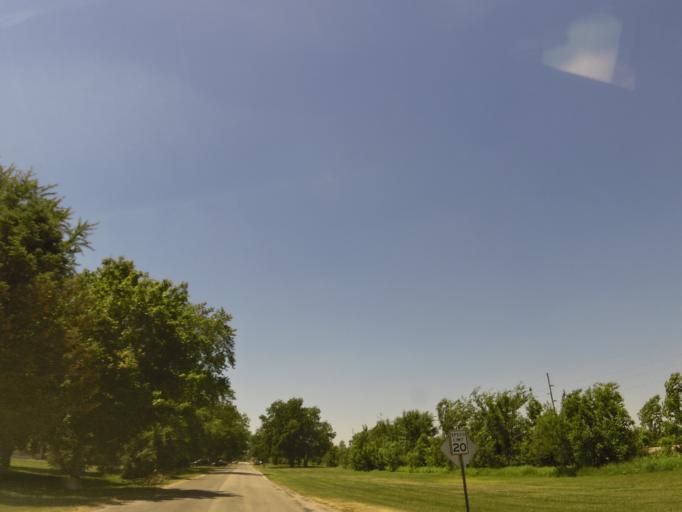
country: US
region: Illinois
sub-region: Livingston County
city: Chatsworth
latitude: 40.7585
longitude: -88.1837
